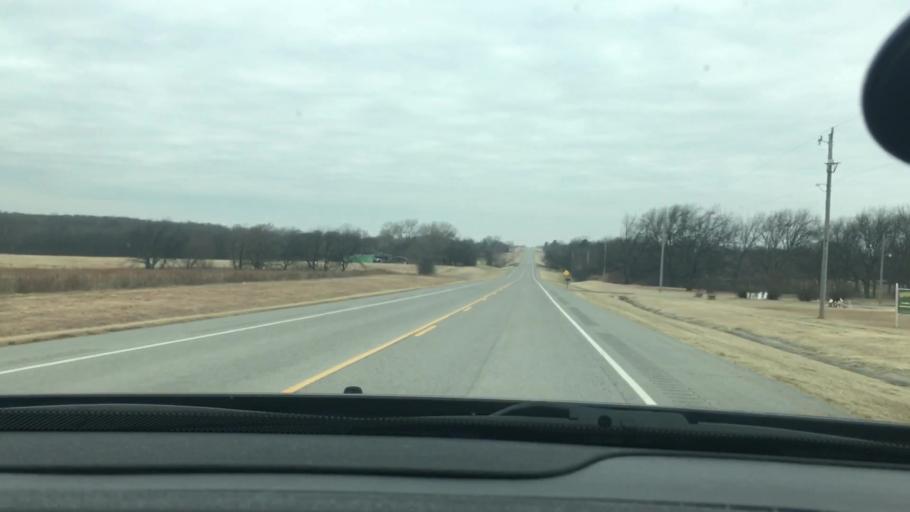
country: US
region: Oklahoma
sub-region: Murray County
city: Davis
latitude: 34.4925
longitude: -97.3746
